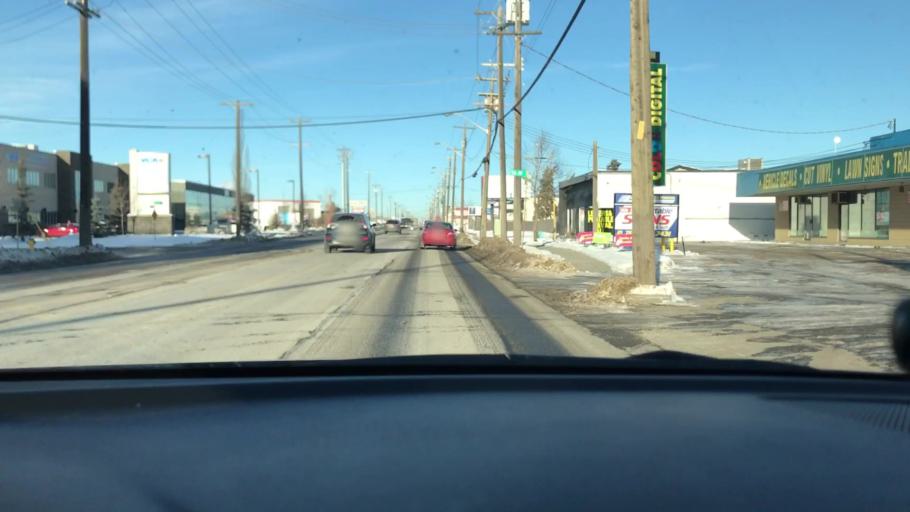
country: CA
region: Alberta
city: Edmonton
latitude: 53.4914
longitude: -113.4861
